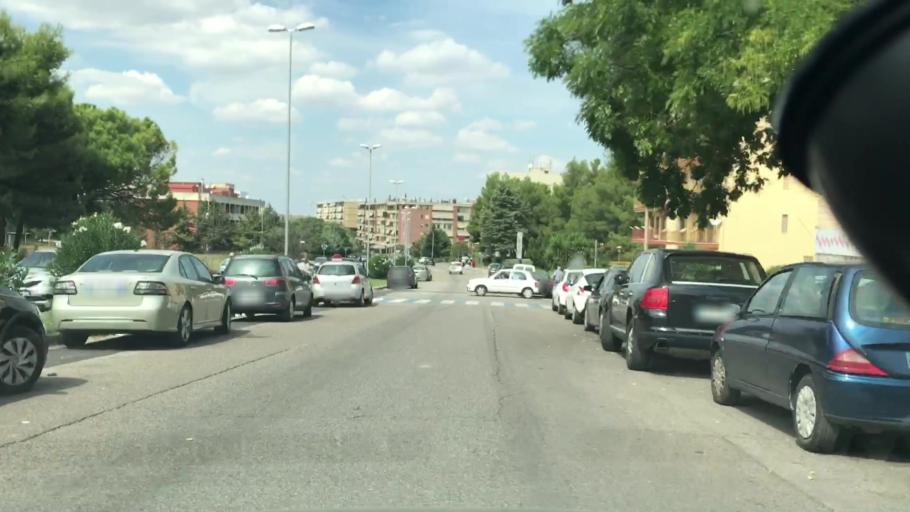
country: IT
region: Basilicate
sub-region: Provincia di Matera
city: Matera
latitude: 40.6752
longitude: 16.5839
